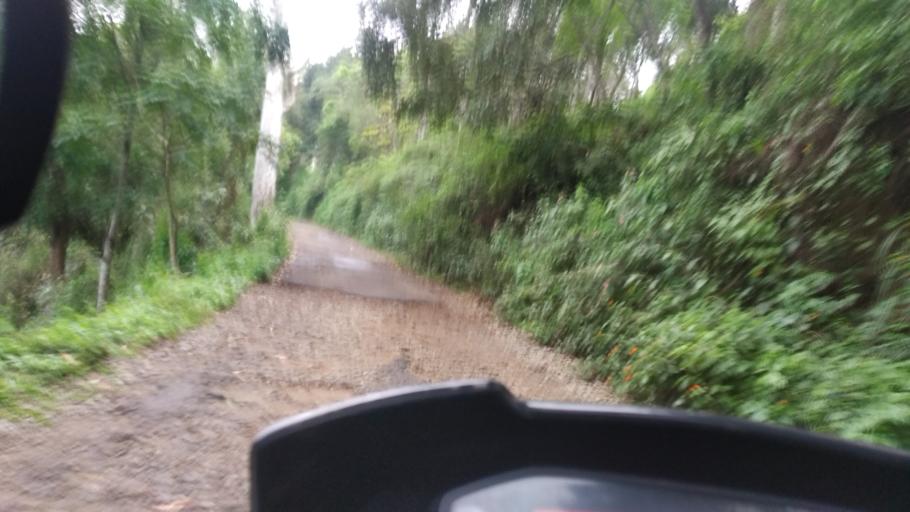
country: IN
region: Tamil Nadu
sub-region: Theni
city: Gudalur
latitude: 9.5526
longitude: 77.0641
